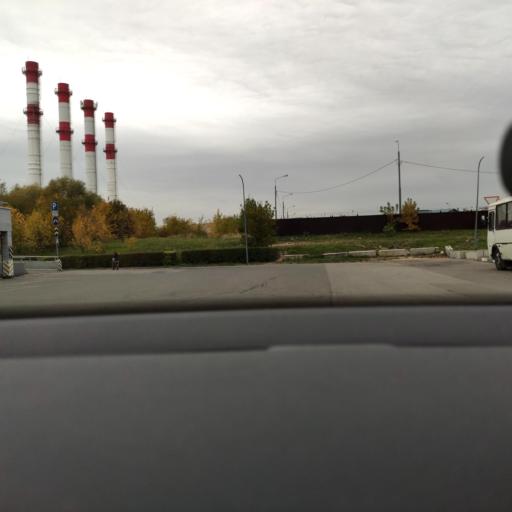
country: RU
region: Moscow
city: Otradnoye
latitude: 55.8525
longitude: 37.5988
